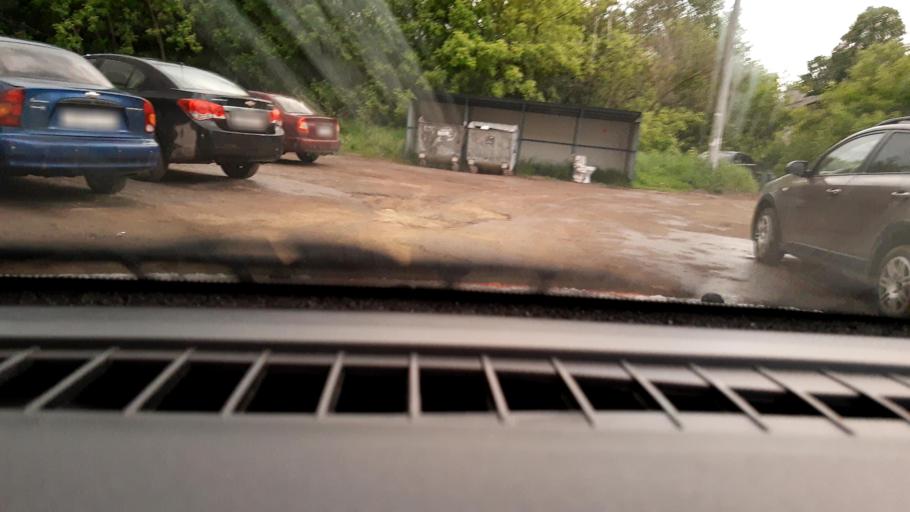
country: RU
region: Nizjnij Novgorod
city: Neklyudovo
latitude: 56.3479
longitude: 43.9085
